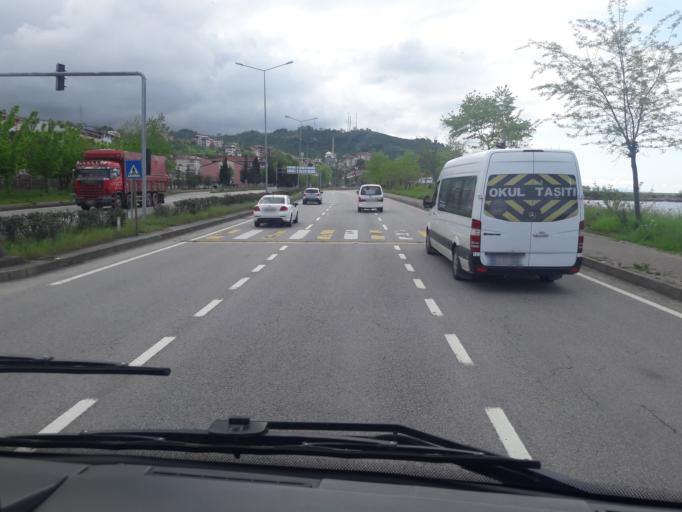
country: TR
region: Giresun
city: Piraziz
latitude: 40.9534
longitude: 38.1290
